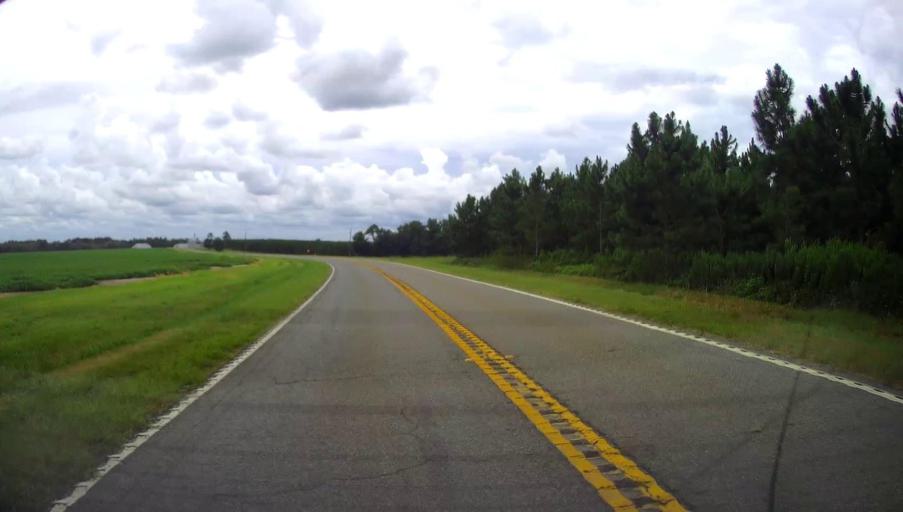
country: US
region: Georgia
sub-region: Dooly County
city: Unadilla
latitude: 32.2648
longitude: -83.8113
